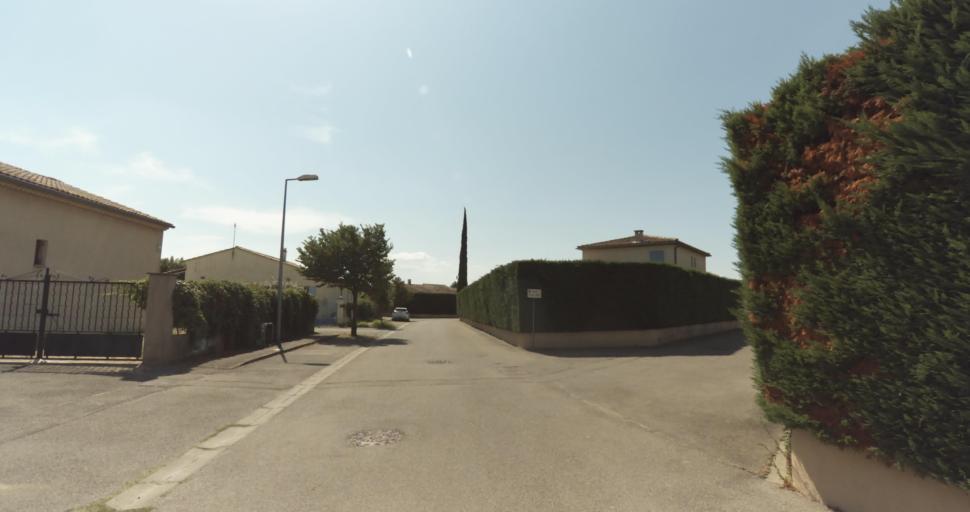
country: FR
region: Provence-Alpes-Cote d'Azur
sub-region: Departement du Vaucluse
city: Monteux
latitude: 44.0338
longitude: 4.9854
